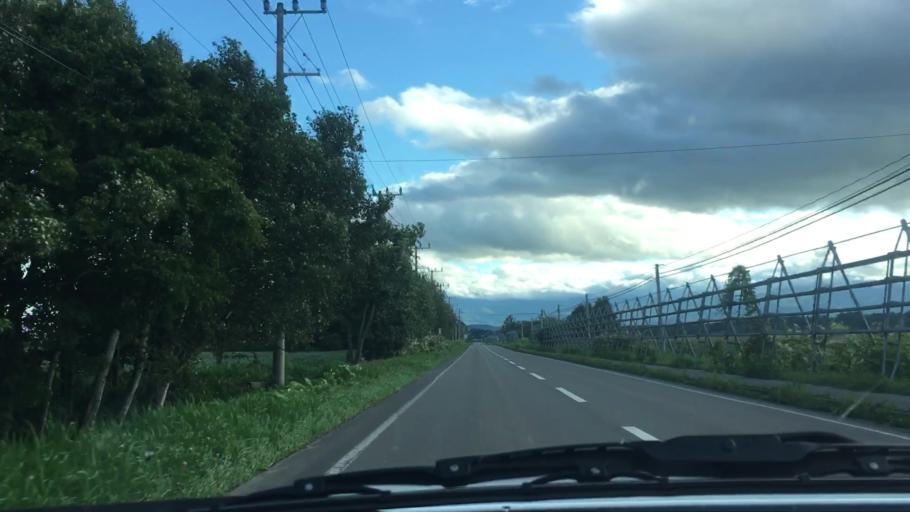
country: JP
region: Hokkaido
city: Otofuke
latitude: 43.1422
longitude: 142.8964
